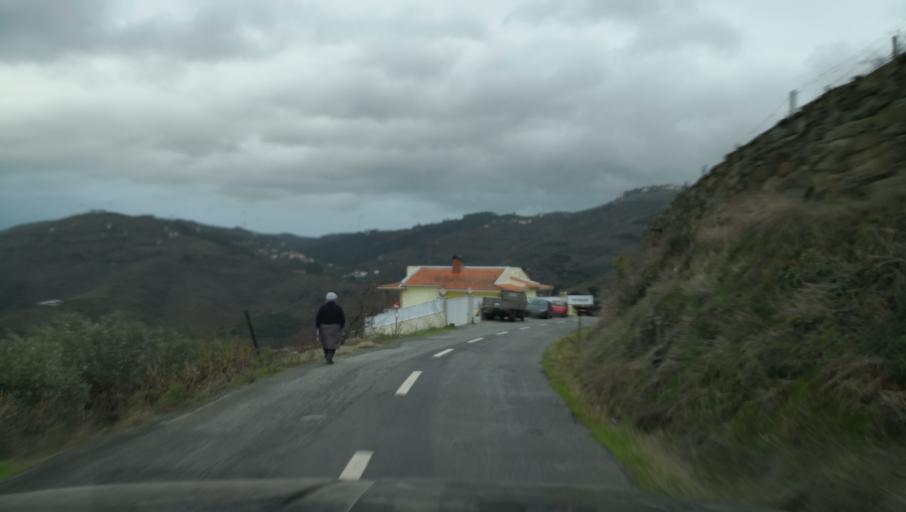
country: PT
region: Vila Real
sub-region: Santa Marta de Penaguiao
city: Santa Marta de Penaguiao
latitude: 41.2210
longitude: -7.7543
